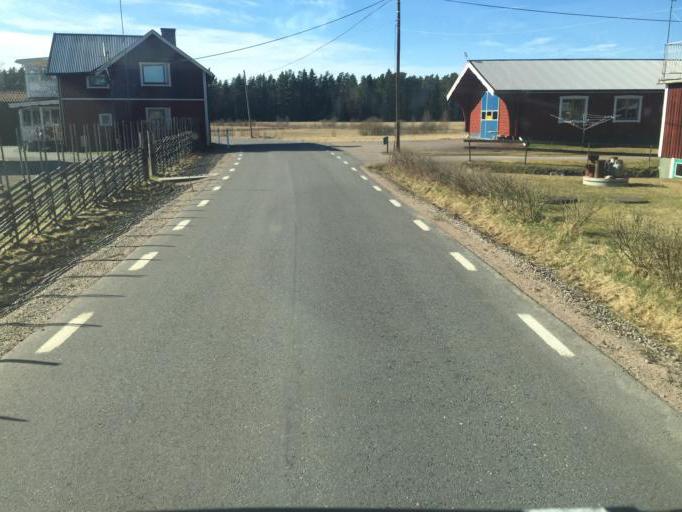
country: SE
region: Dalarna
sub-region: Vansbro Kommun
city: Vansbro
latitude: 60.4618
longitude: 13.9768
